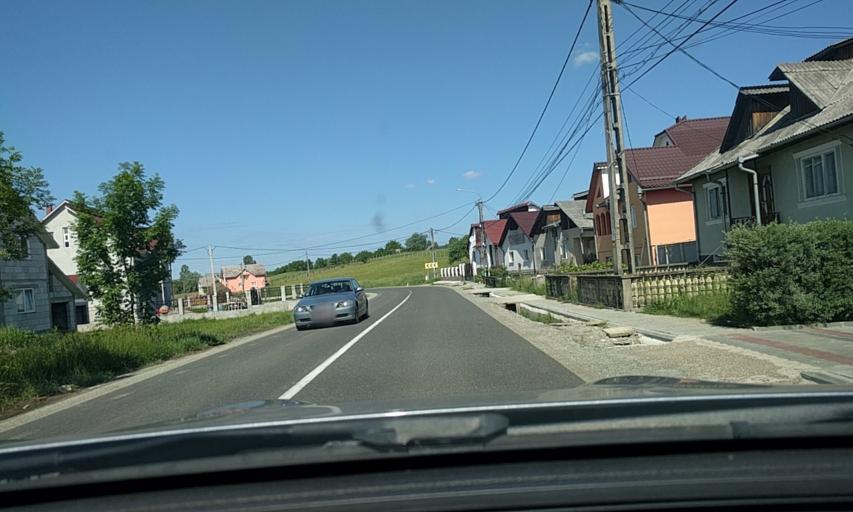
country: RO
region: Bistrita-Nasaud
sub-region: Comuna Dumitra
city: Dumitra
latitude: 47.2316
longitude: 24.4538
